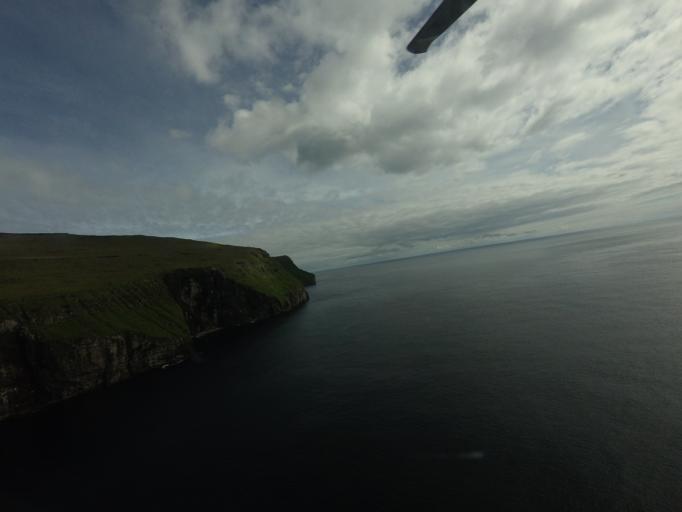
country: FO
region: Nordoyar
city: Klaksvik
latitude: 62.3135
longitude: -6.3071
